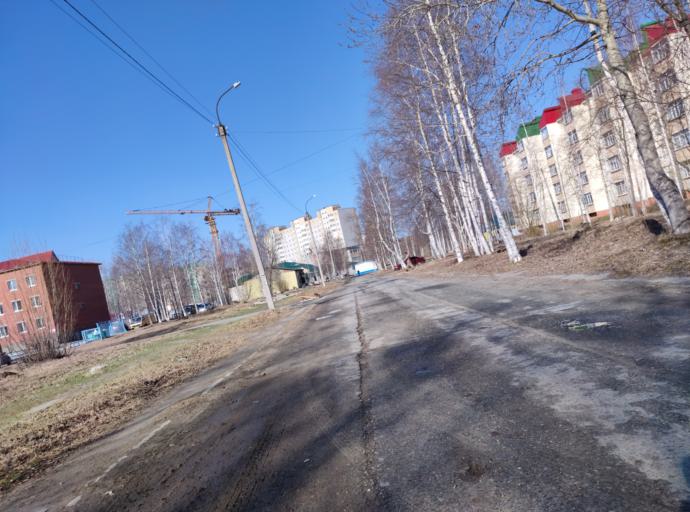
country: RU
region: Khanty-Mansiyskiy Avtonomnyy Okrug
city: Langepas
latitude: 61.2514
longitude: 75.1708
